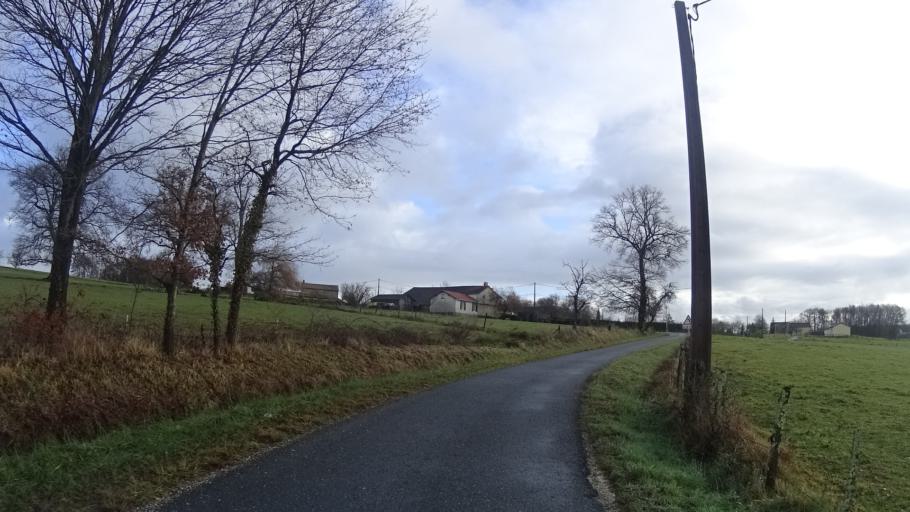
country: FR
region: Aquitaine
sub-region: Departement de la Dordogne
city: Thiviers
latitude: 45.4032
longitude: 0.9569
